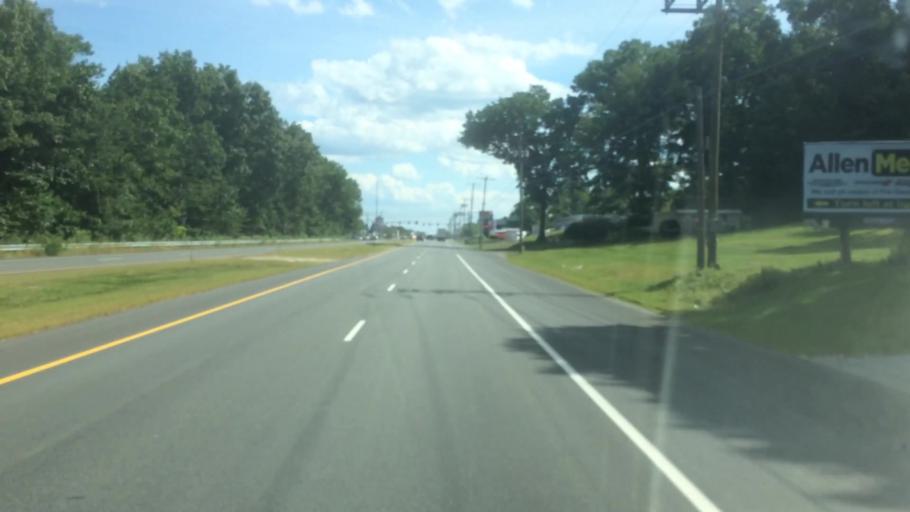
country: US
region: New Hampshire
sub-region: Hillsborough County
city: Hudson
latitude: 42.7324
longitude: -71.4508
